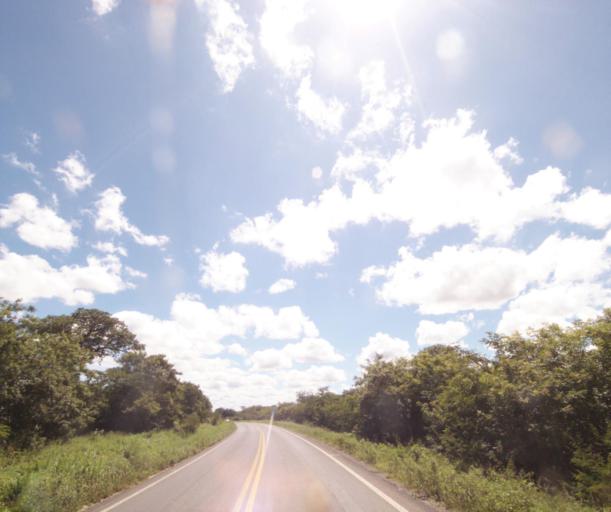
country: BR
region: Bahia
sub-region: Sao Felix Do Coribe
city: Santa Maria da Vitoria
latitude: -13.4069
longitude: -44.1587
